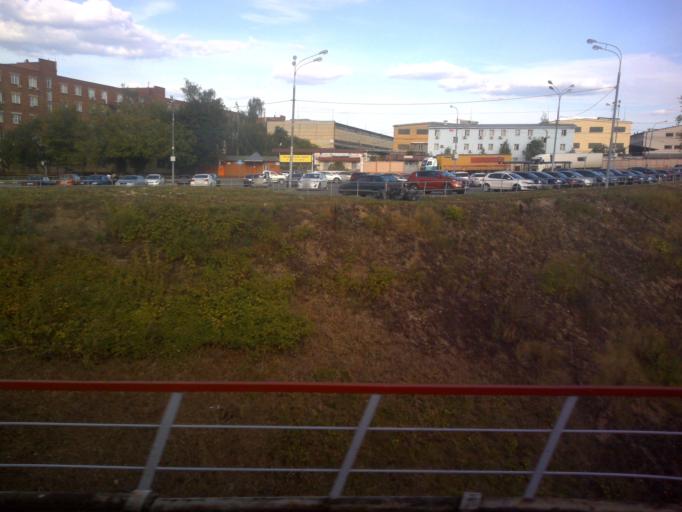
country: RU
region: Moscow
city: Nagornyy
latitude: 55.6326
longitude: 37.6272
